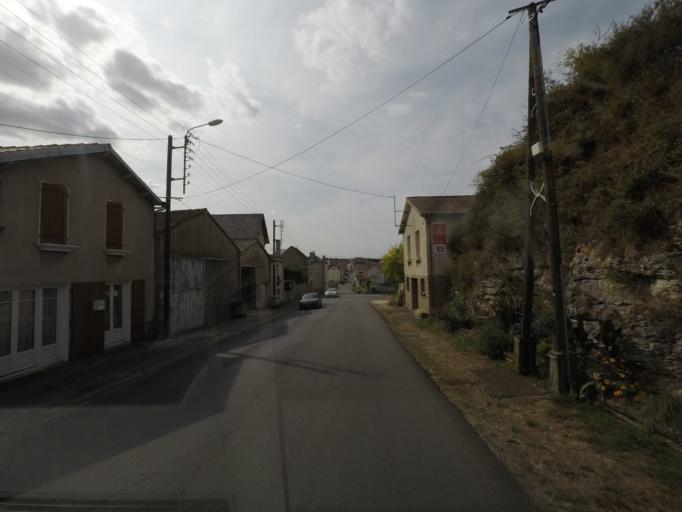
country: FR
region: Poitou-Charentes
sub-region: Departement de la Charente
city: Ruffec
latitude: 46.0278
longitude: 0.2071
